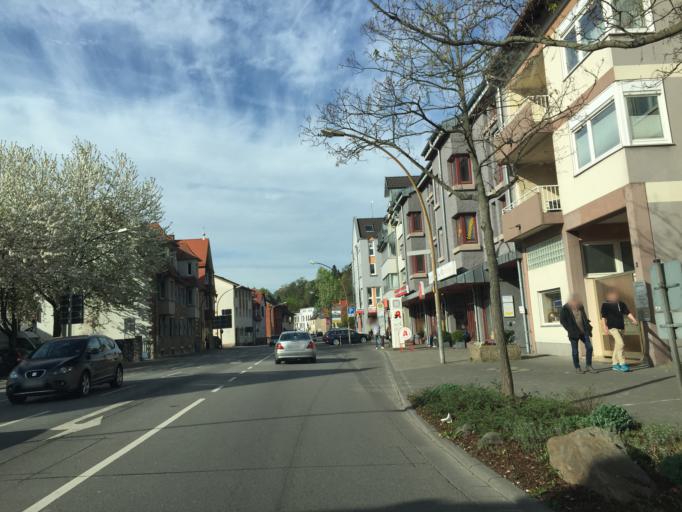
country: DE
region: Hesse
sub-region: Regierungsbezirk Darmstadt
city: Heppenheim an der Bergstrasse
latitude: 49.6433
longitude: 8.6391
